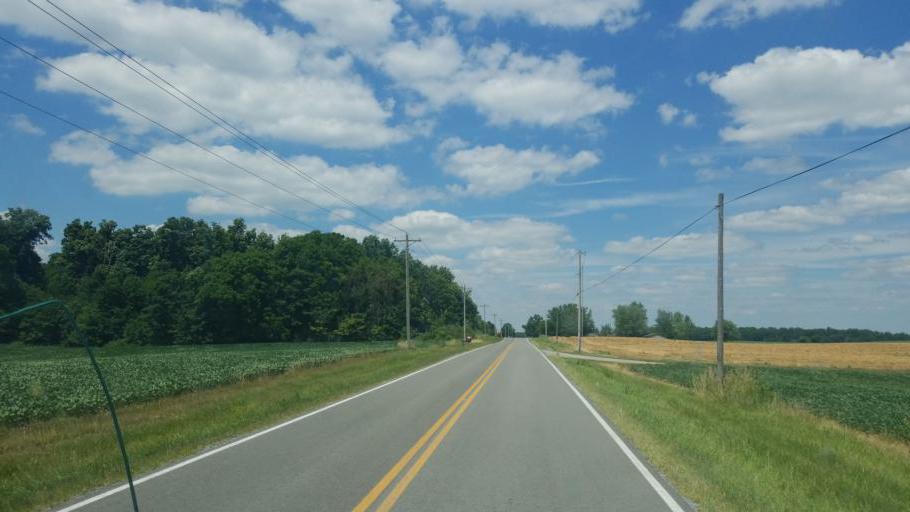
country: US
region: Ohio
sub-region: Williams County
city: Edgerton
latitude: 41.4202
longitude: -84.7101
